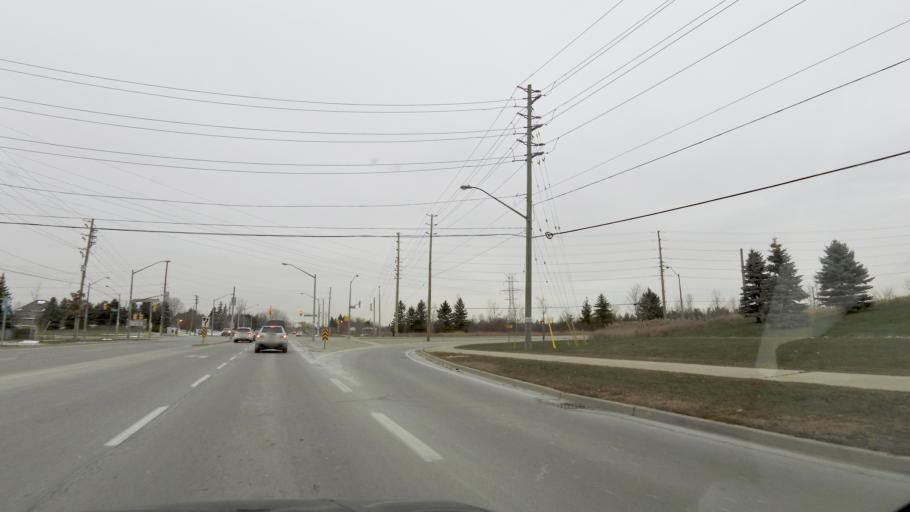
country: CA
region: Ontario
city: Vaughan
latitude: 43.8319
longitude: -79.6167
